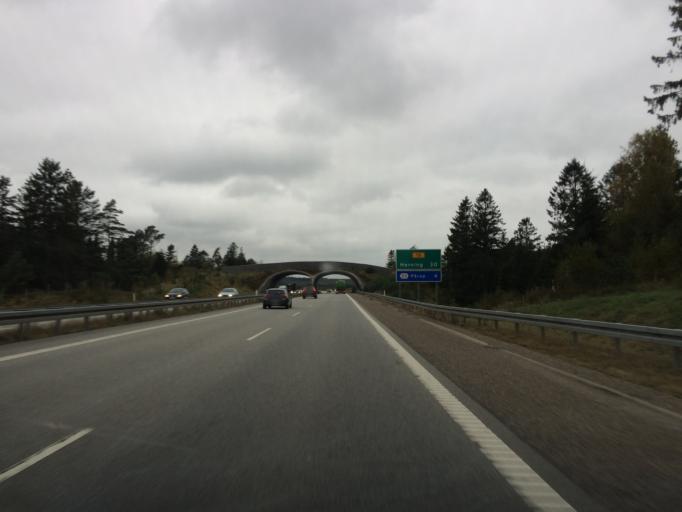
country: DK
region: Central Jutland
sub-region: Silkeborg Kommune
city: Silkeborg
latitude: 56.1447
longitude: 9.4273
